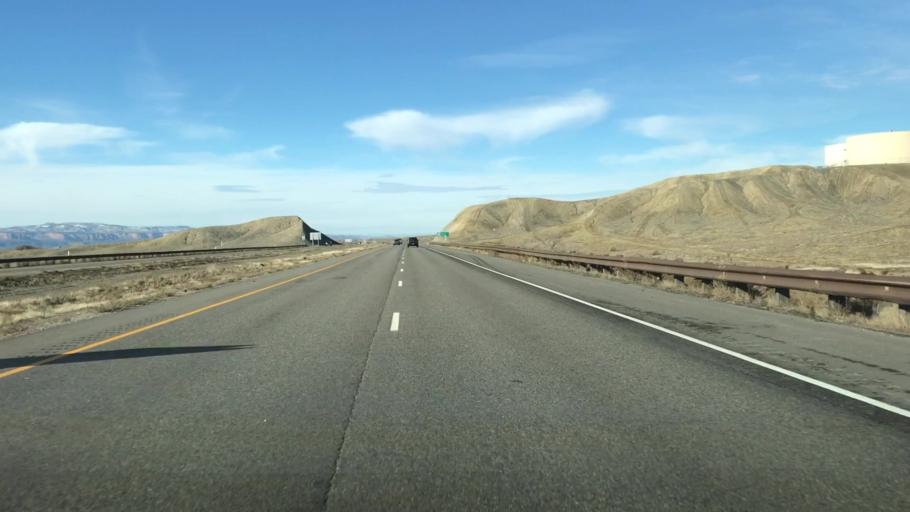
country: US
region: Colorado
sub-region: Mesa County
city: Clifton
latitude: 39.1025
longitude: -108.4574
